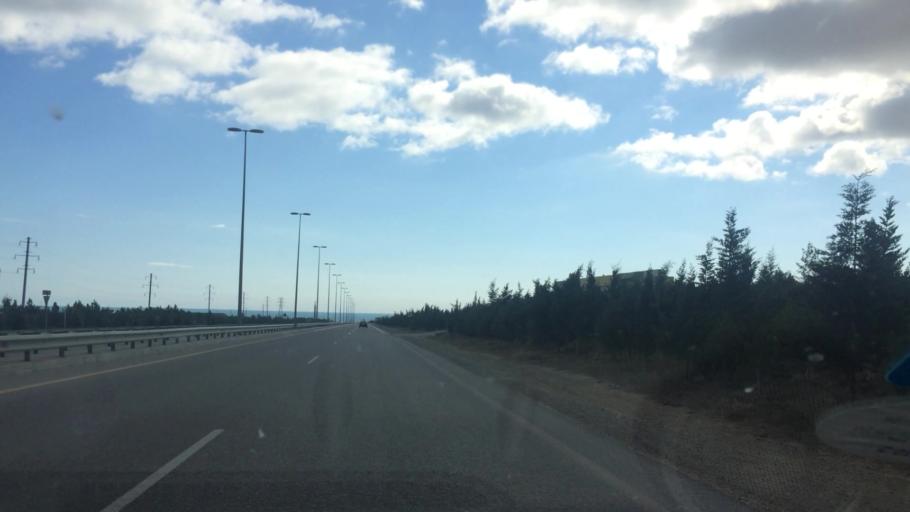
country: AZ
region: Baki
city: Zyrya
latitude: 40.4043
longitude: 50.3036
